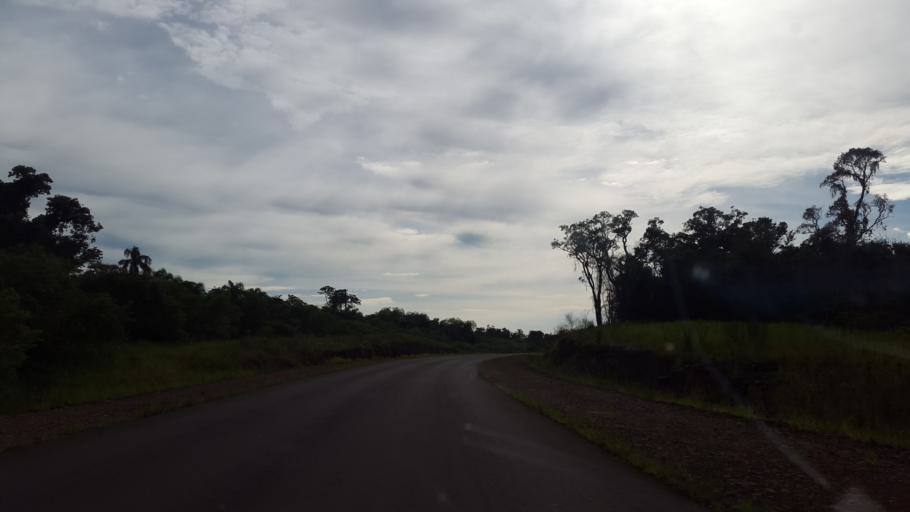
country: AR
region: Misiones
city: Bernardo de Irigoyen
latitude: -26.4204
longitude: -53.8329
